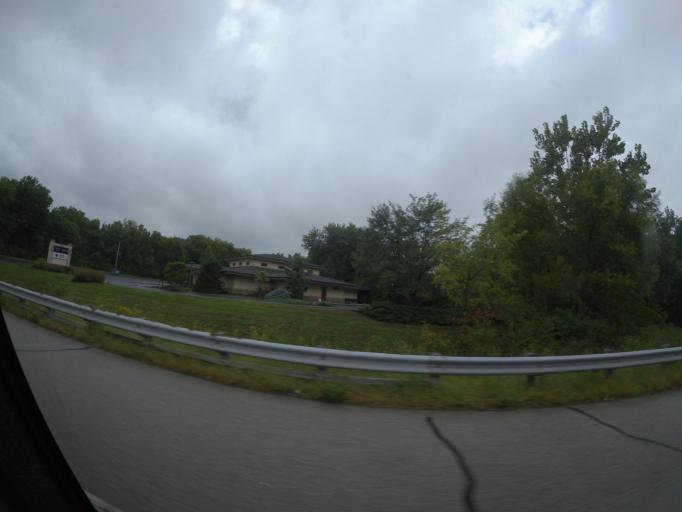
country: US
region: Indiana
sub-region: Montgomery County
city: Crawfordsville
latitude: 40.0620
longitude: -86.9086
